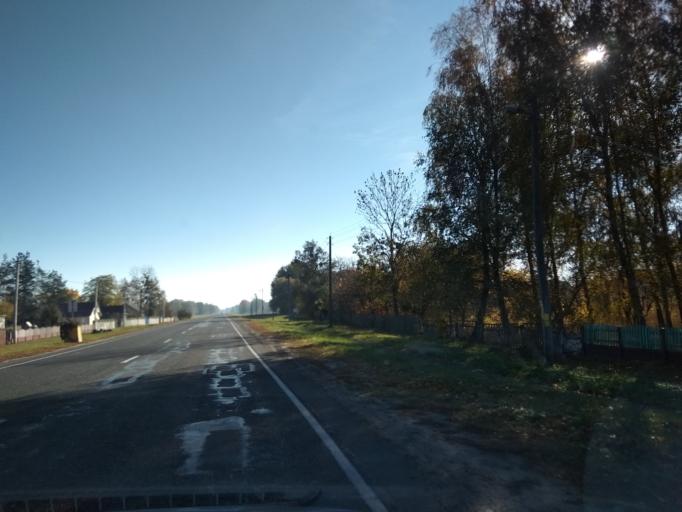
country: BY
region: Brest
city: Malaryta
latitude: 51.8330
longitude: 24.2639
